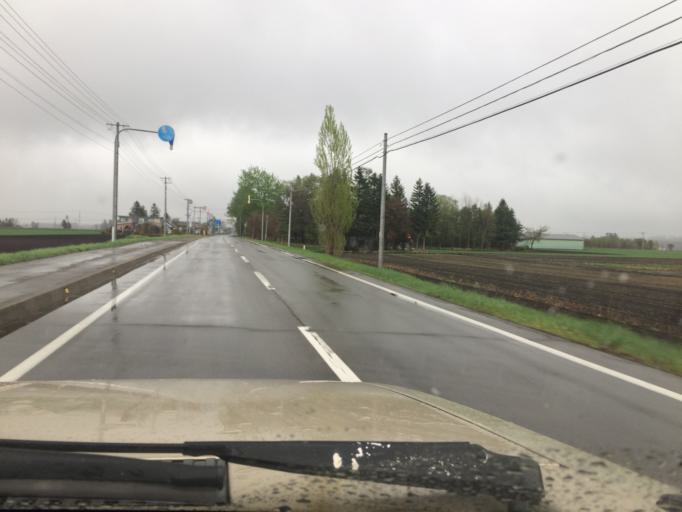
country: JP
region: Hokkaido
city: Obihiro
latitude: 42.8624
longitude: 143.0131
